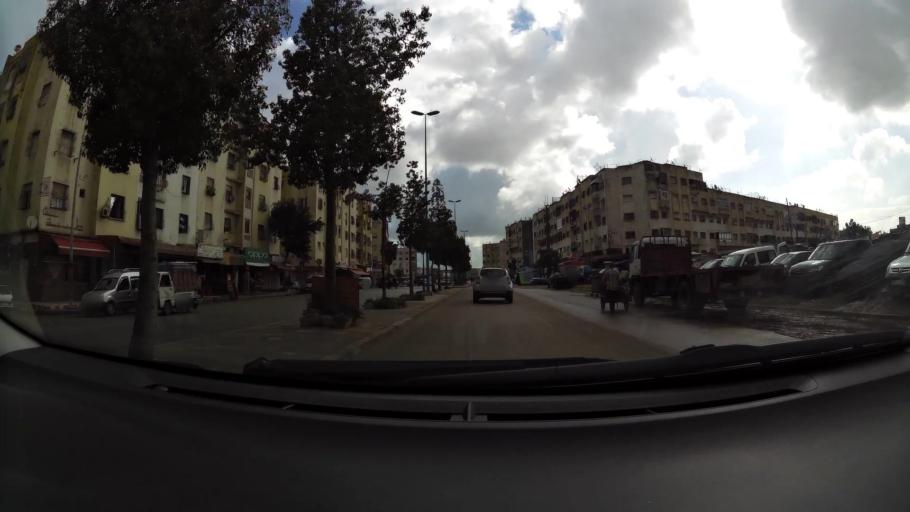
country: MA
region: Grand Casablanca
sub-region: Mediouna
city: Tit Mellil
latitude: 33.5904
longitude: -7.5184
